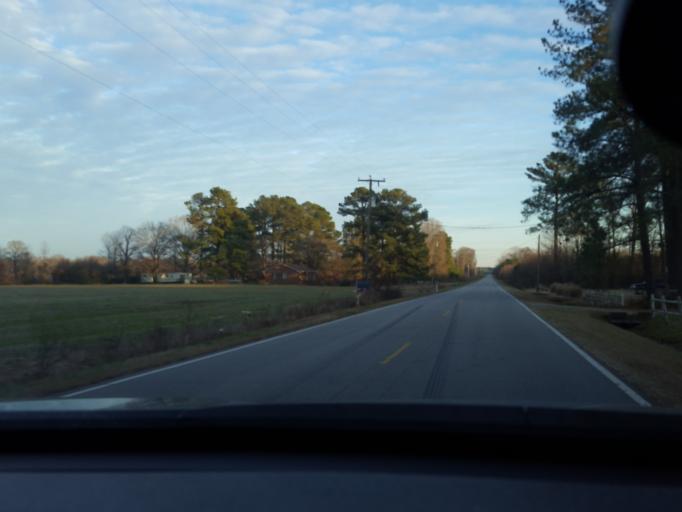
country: US
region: North Carolina
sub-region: Hertford County
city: Murfreesboro
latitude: 36.2845
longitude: -77.1714
